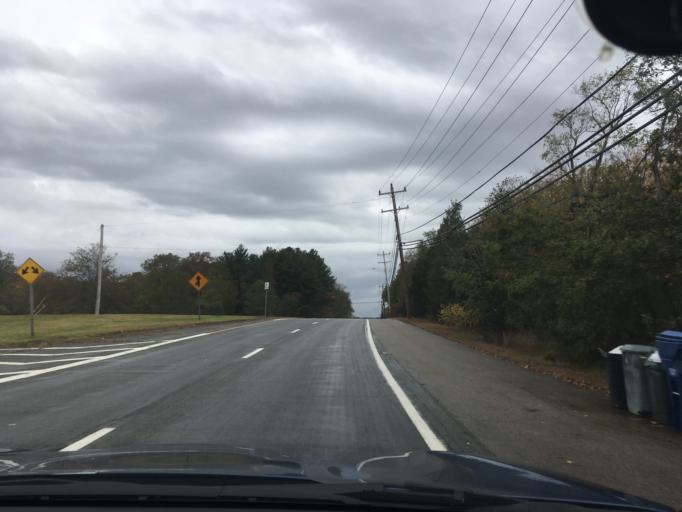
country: US
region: Rhode Island
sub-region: Kent County
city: East Greenwich
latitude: 41.6306
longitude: -71.4730
